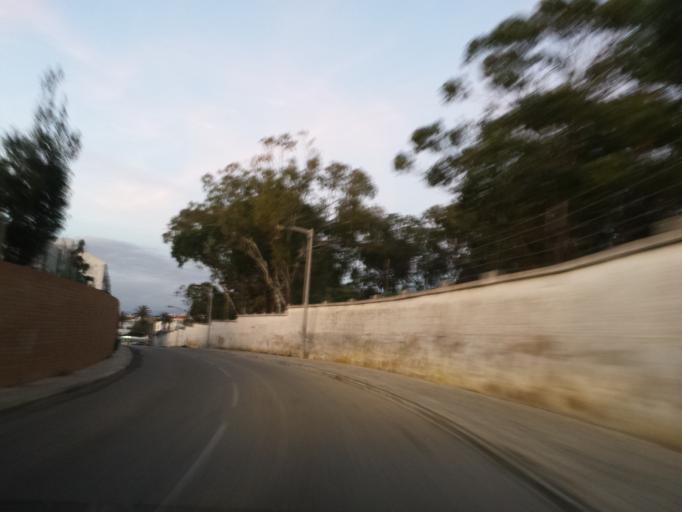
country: PT
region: Faro
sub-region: Lagos
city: Lagos
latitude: 37.0931
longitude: -8.6721
